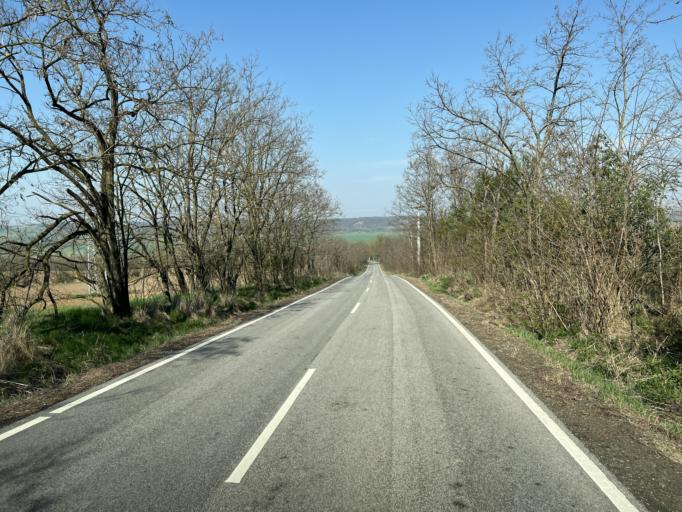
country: HU
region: Pest
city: Szob
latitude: 47.9401
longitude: 18.7829
